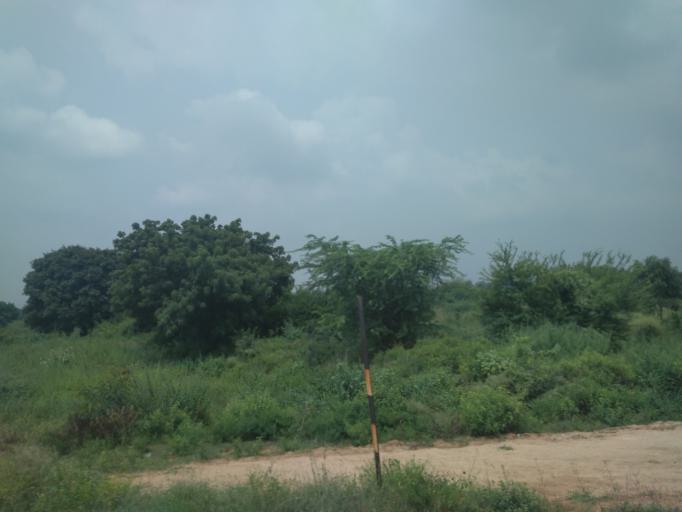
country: IN
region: Telangana
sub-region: Warangal
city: Jangaon
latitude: 17.6605
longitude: 79.0789
